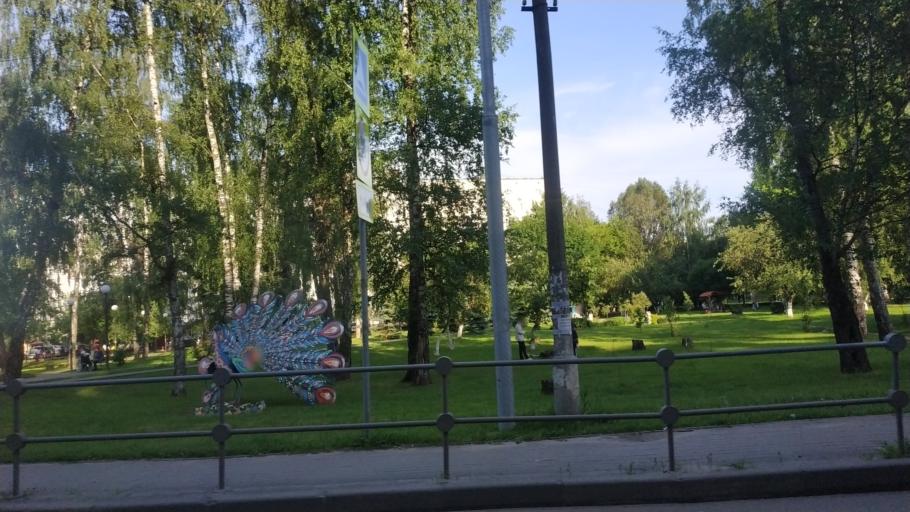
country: RU
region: Moskovskaya
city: Saltykovka
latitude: 55.7311
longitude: 37.9651
